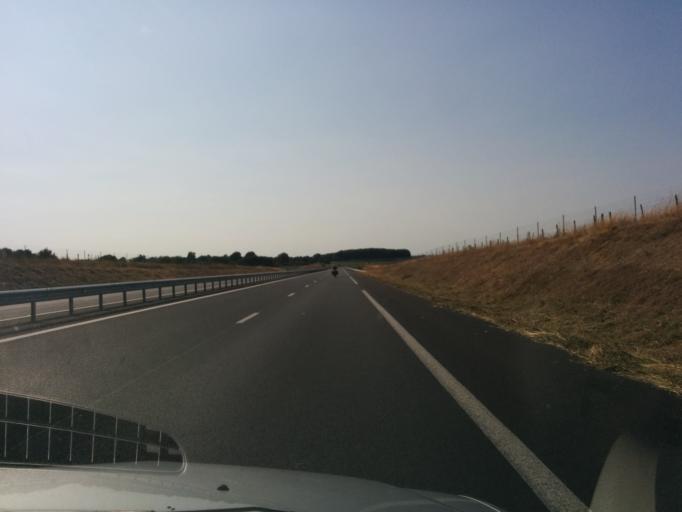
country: FR
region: Poitou-Charentes
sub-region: Departement des Deux-Sevres
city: Nueil-les-Aubiers
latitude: 46.8787
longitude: -0.5915
